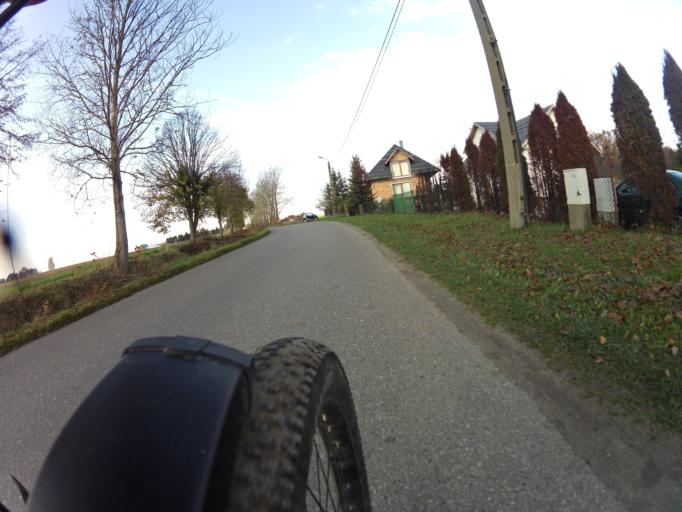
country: PL
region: Pomeranian Voivodeship
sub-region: Powiat pucki
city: Krokowa
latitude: 54.7548
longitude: 18.1848
